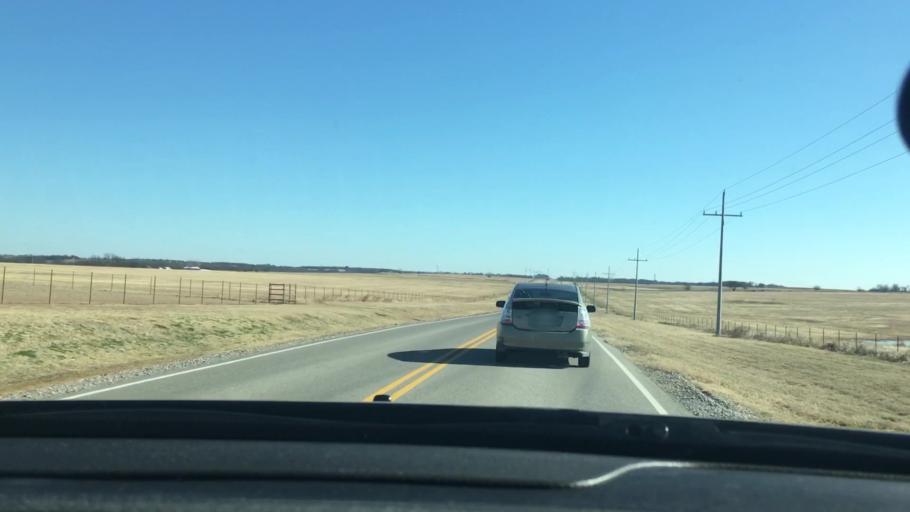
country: US
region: Oklahoma
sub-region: Murray County
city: Davis
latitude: 34.4774
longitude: -97.0980
